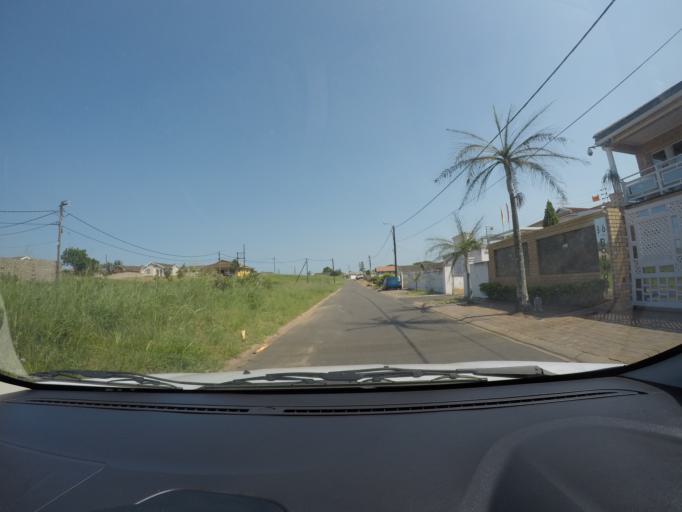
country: ZA
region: KwaZulu-Natal
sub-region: uThungulu District Municipality
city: Richards Bay
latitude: -28.7257
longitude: 32.0366
